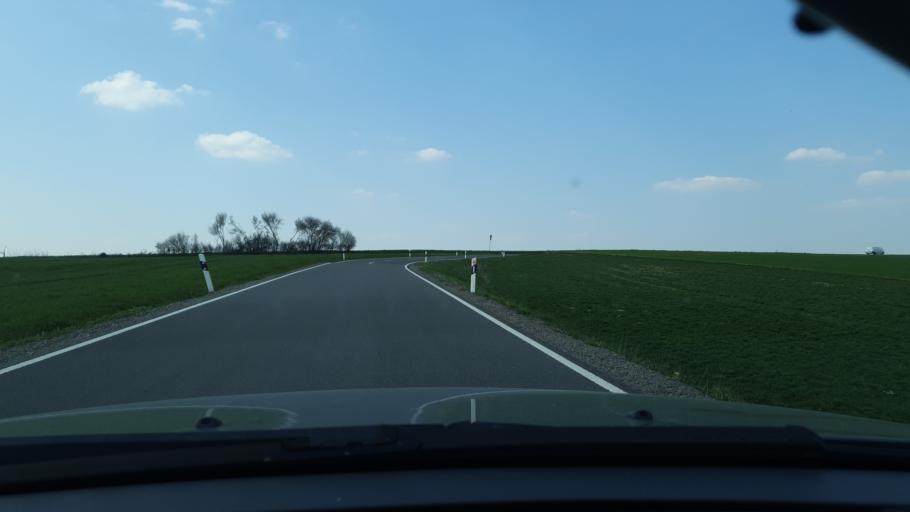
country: DE
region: Rheinland-Pfalz
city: Martinshohe
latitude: 49.3521
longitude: 7.4882
